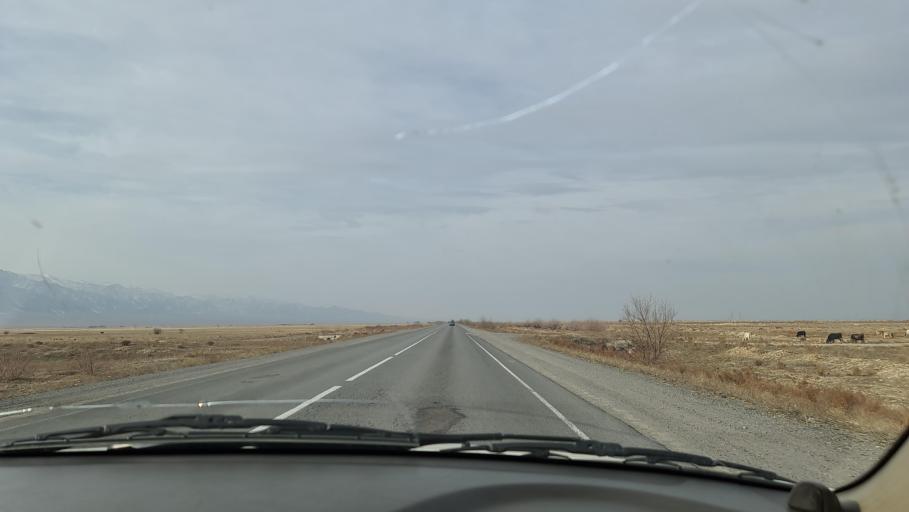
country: KG
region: Chuy
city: Tokmok
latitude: 43.3419
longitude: 75.5476
